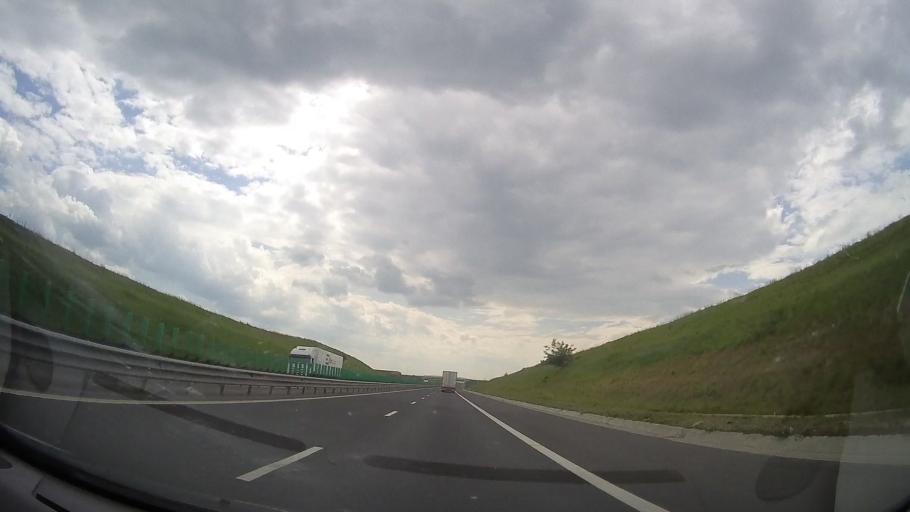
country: RO
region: Alba
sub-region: Comuna Saliste
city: Salistea
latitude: 45.9459
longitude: 23.4138
